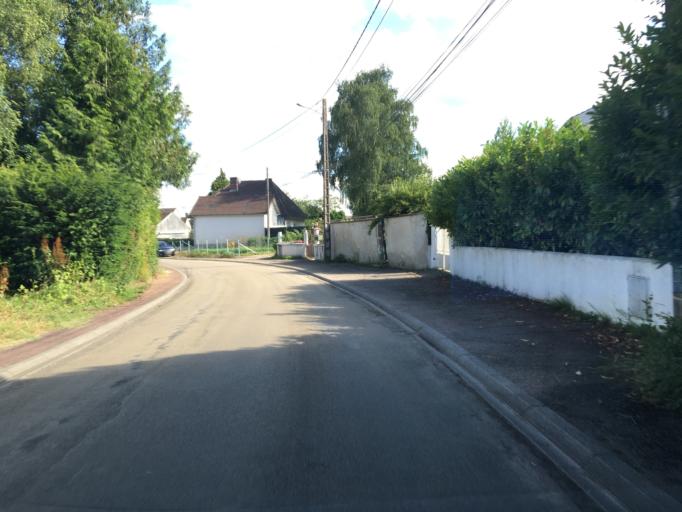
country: FR
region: Bourgogne
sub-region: Departement de l'Yonne
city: Appoigny
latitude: 47.8777
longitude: 3.5212
